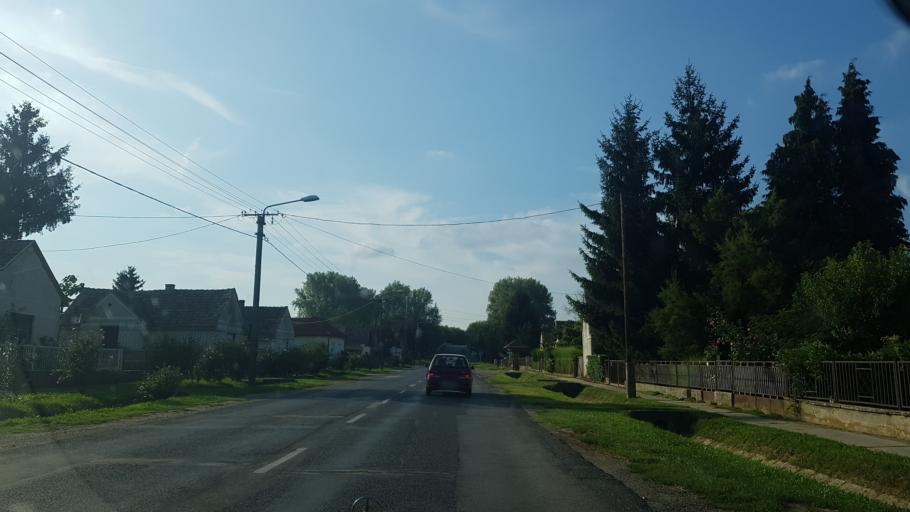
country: HU
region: Somogy
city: Segesd
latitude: 46.2888
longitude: 17.3597
